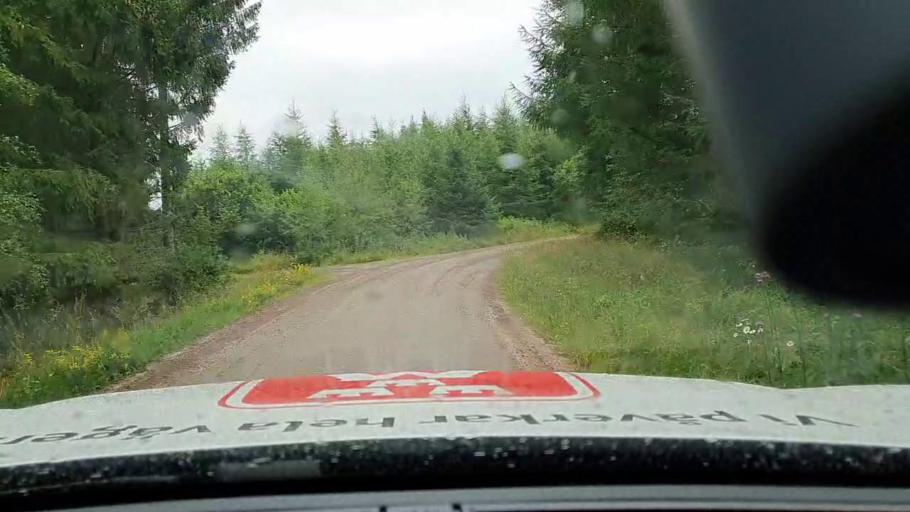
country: SE
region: Vaestra Goetaland
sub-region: Skara Kommun
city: Axvall
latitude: 58.4604
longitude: 13.6555
